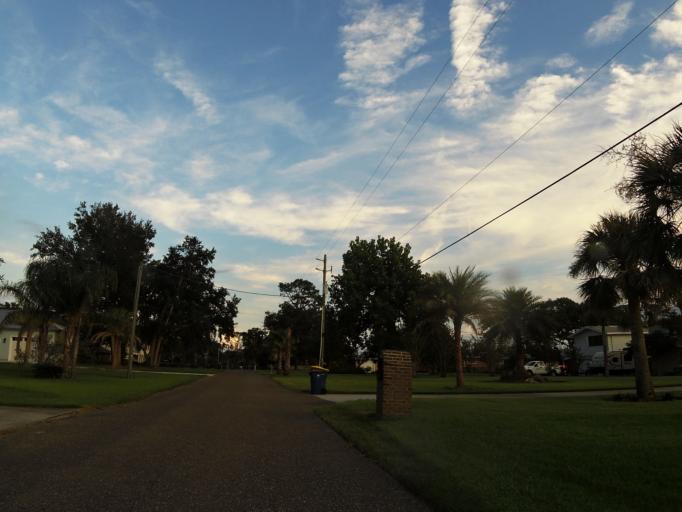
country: US
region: Florida
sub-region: Duval County
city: Atlantic Beach
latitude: 30.3967
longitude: -81.5040
